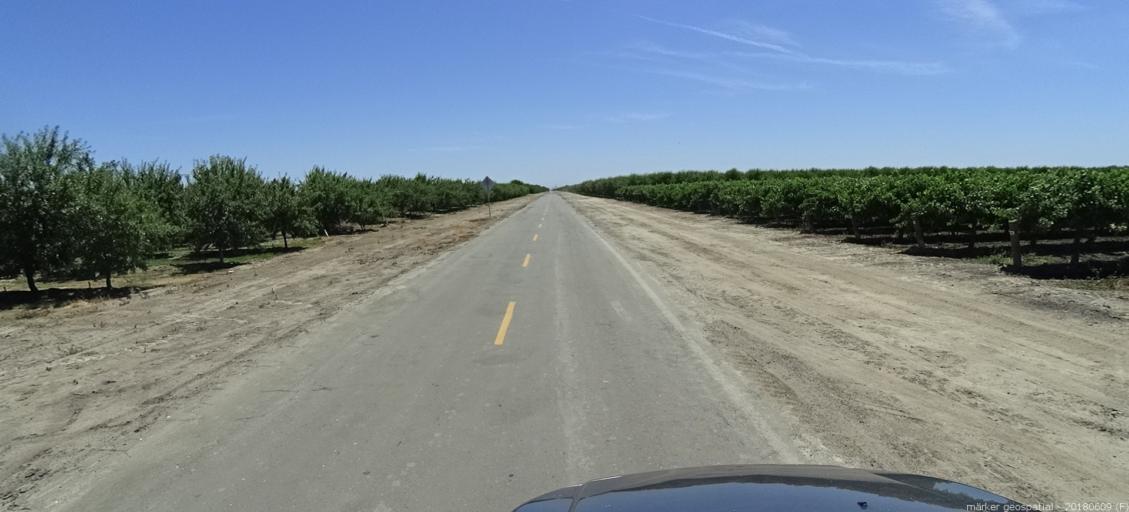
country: US
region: California
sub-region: Madera County
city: Fairmead
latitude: 36.9382
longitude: -120.2001
